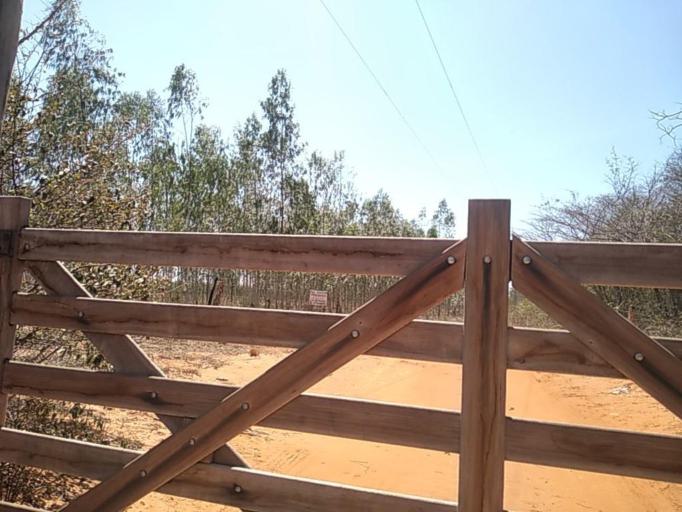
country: BR
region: Bahia
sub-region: Caetite
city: Caetite
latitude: -13.9785
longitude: -42.5110
